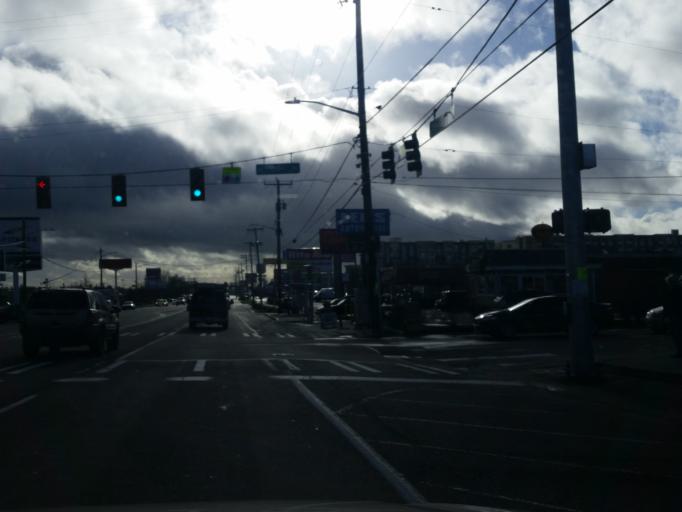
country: US
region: Washington
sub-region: King County
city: Shoreline
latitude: 47.7271
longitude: -122.3451
